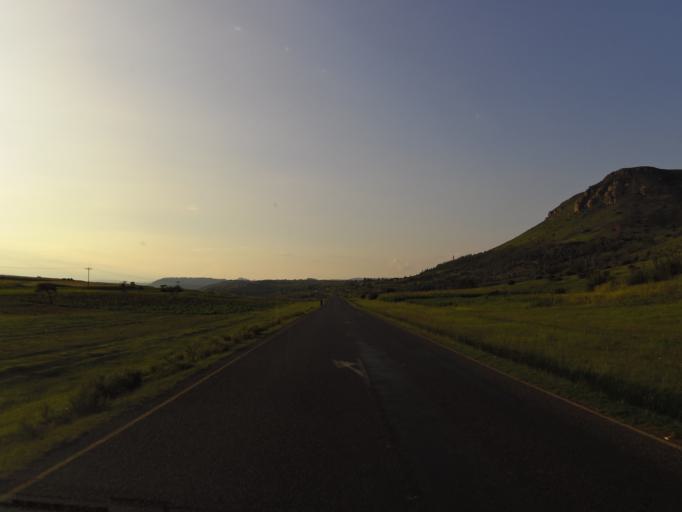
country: LS
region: Leribe
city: Leribe
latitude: -28.9785
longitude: 28.1784
